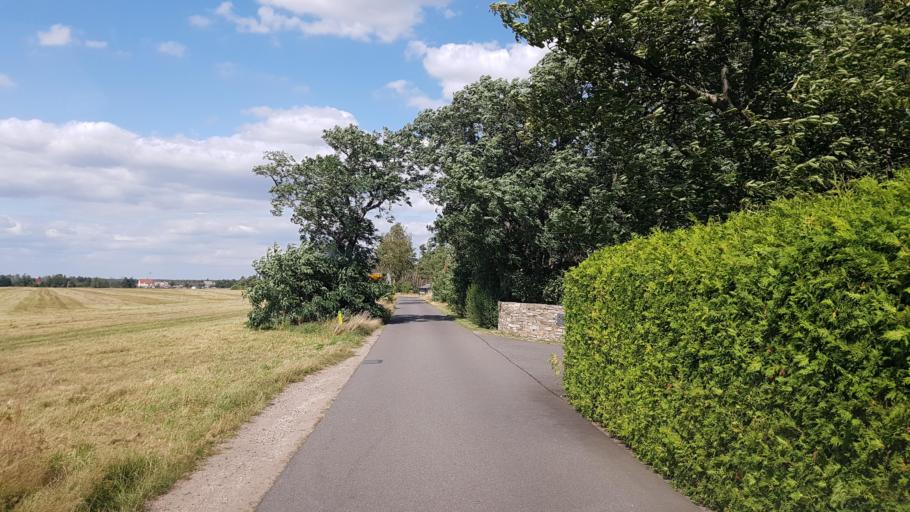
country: DE
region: Brandenburg
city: Muhlberg
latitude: 51.4556
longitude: 13.2991
